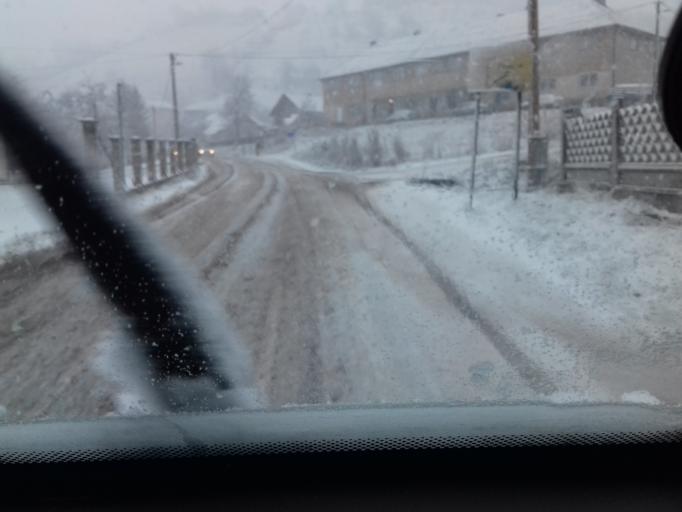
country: BA
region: Federation of Bosnia and Herzegovina
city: Lokvine
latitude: 44.2301
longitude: 17.8476
